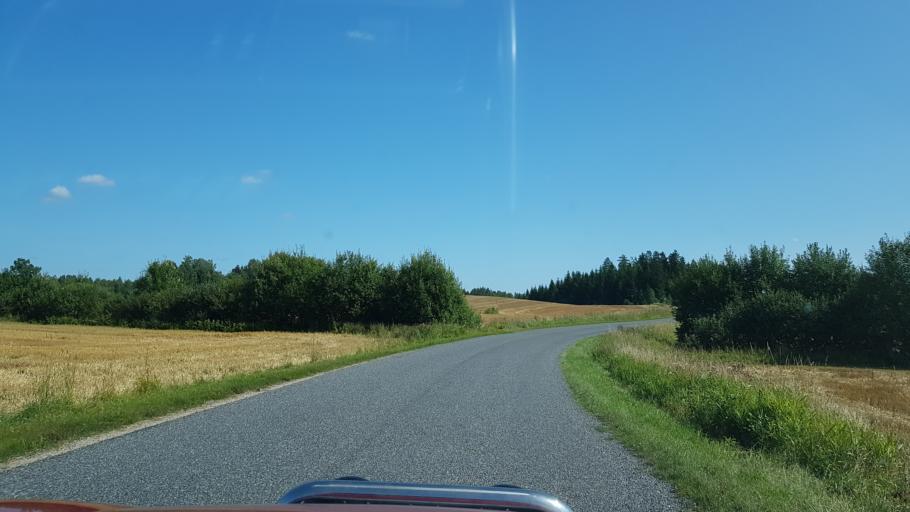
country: EE
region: Vorumaa
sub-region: Voru linn
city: Voru
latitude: 57.7540
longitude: 27.2871
